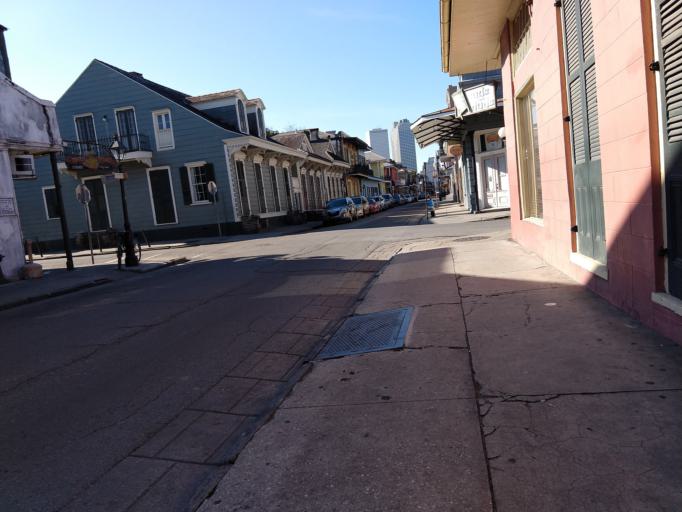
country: US
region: Louisiana
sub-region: Orleans Parish
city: New Orleans
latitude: 29.9620
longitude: -90.0627
